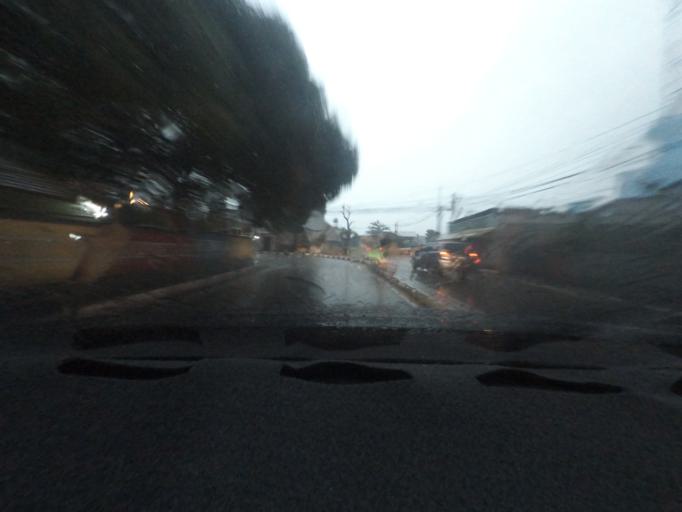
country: ID
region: West Java
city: Bogor
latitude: -6.5911
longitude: 106.7862
